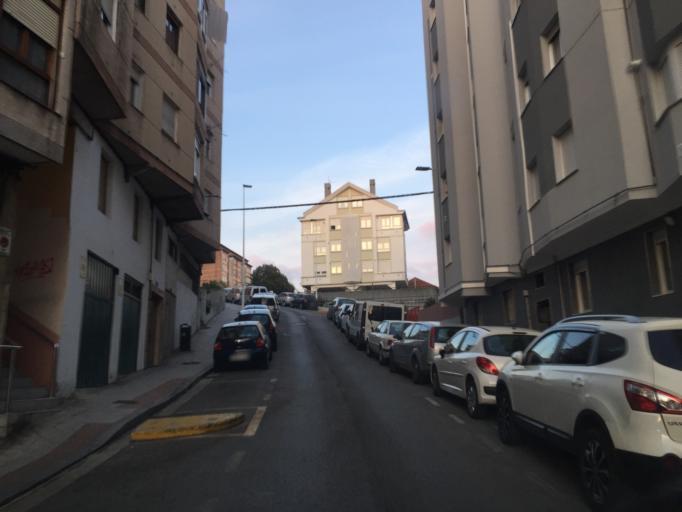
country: ES
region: Cantabria
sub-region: Provincia de Cantabria
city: Santander
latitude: 43.4654
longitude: -3.8024
